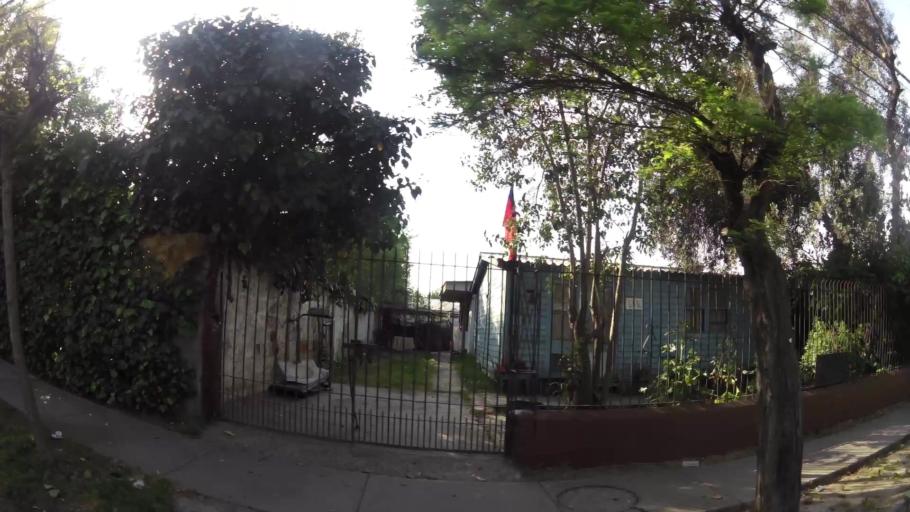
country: CL
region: Santiago Metropolitan
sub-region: Provincia de Santiago
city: Santiago
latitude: -33.5143
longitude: -70.6697
